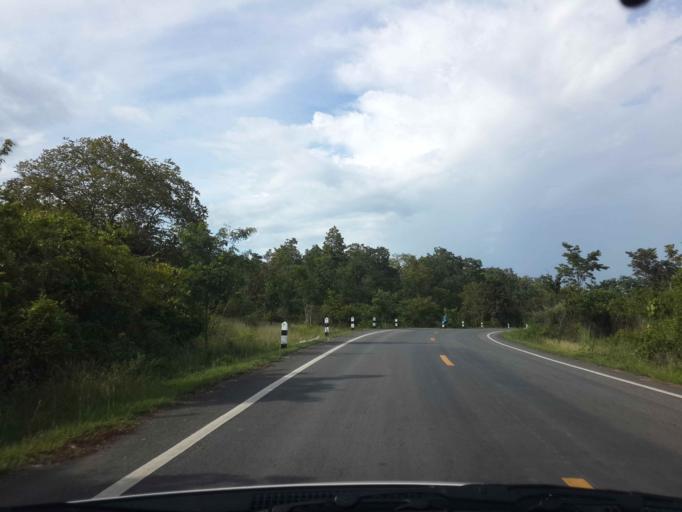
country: TH
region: Kanchanaburi
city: Dan Makham Tia
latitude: 13.8246
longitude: 99.1672
